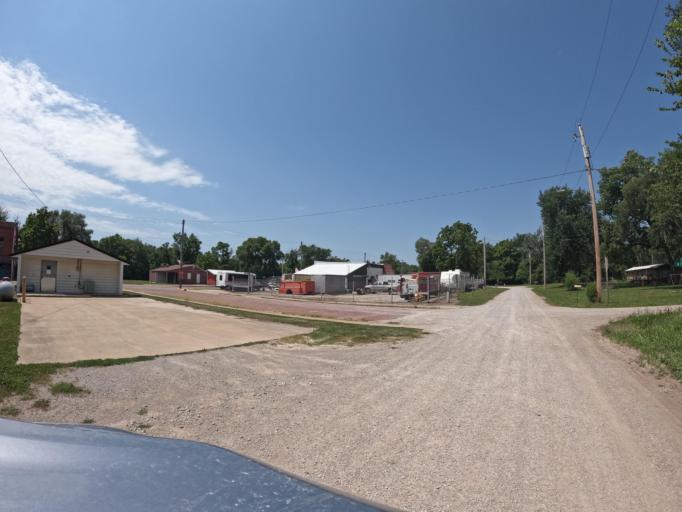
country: US
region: Iowa
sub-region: Appanoose County
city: Centerville
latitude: 40.7781
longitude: -92.9463
